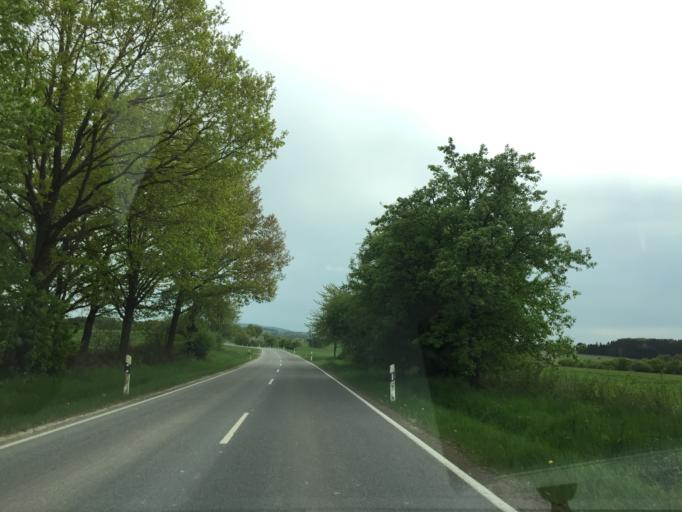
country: DE
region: Rheinland-Pfalz
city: Berod bei Wallmerod
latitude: 50.4776
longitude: 7.9354
